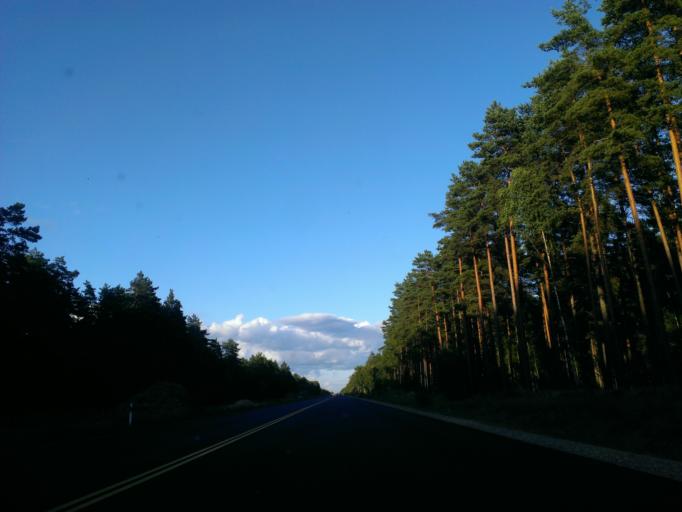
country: LV
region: Adazi
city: Adazi
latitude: 57.0242
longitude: 24.3522
